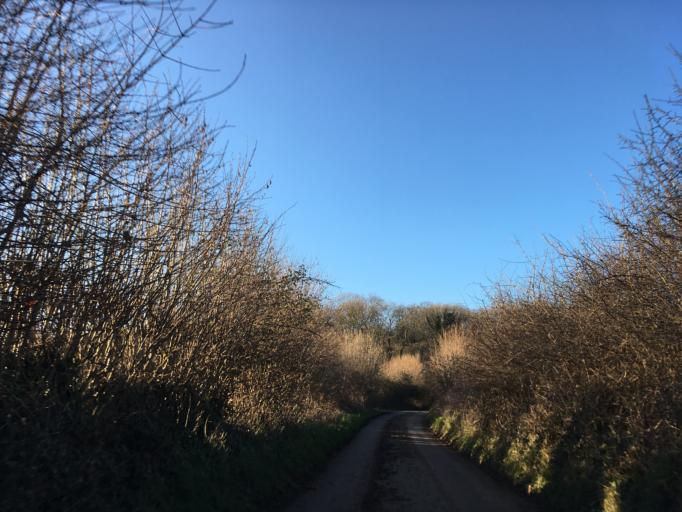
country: GB
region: England
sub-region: South Gloucestershire
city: Tytherington
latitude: 51.6053
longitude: -2.4584
